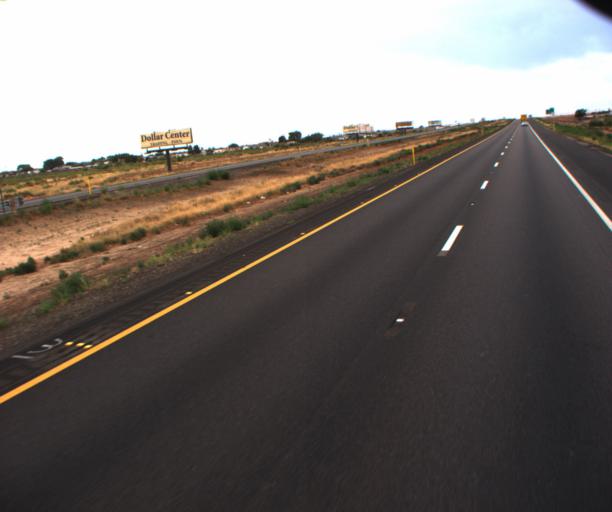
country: US
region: Arizona
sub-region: Navajo County
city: Winslow
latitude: 35.0297
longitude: -110.6846
